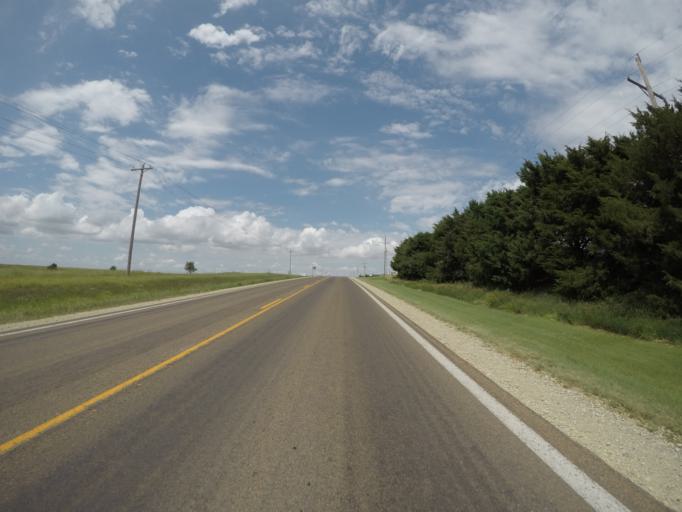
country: US
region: Kansas
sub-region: Rawlins County
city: Atwood
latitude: 39.8289
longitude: -101.0468
